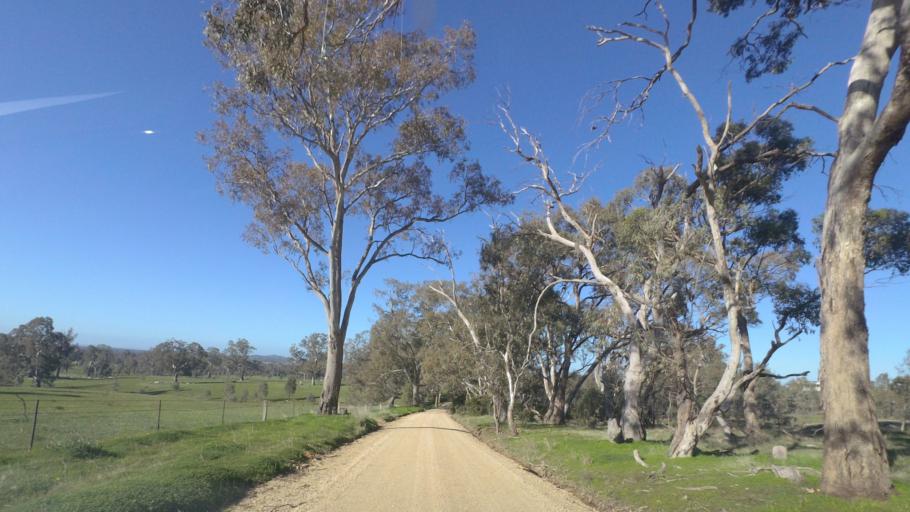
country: AU
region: Victoria
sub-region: Mount Alexander
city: Castlemaine
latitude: -36.9628
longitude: 144.3393
